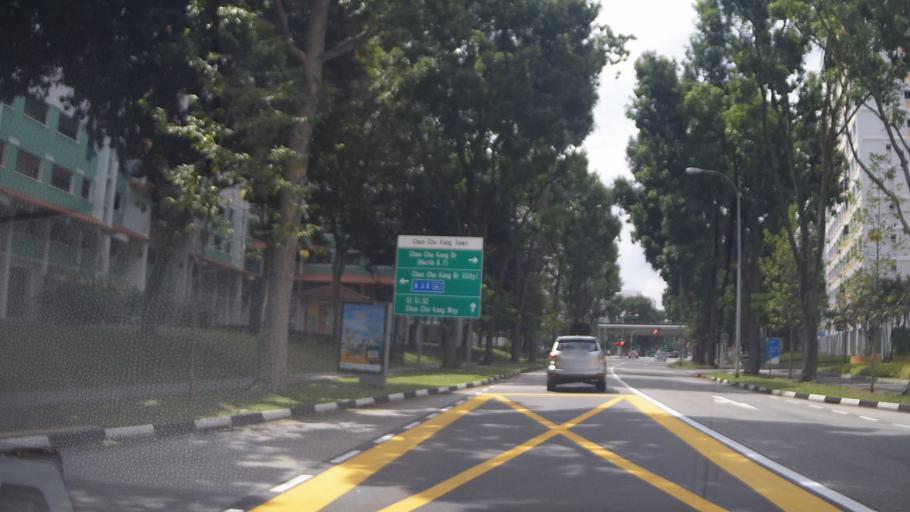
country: MY
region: Johor
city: Johor Bahru
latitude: 1.3919
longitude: 103.7467
